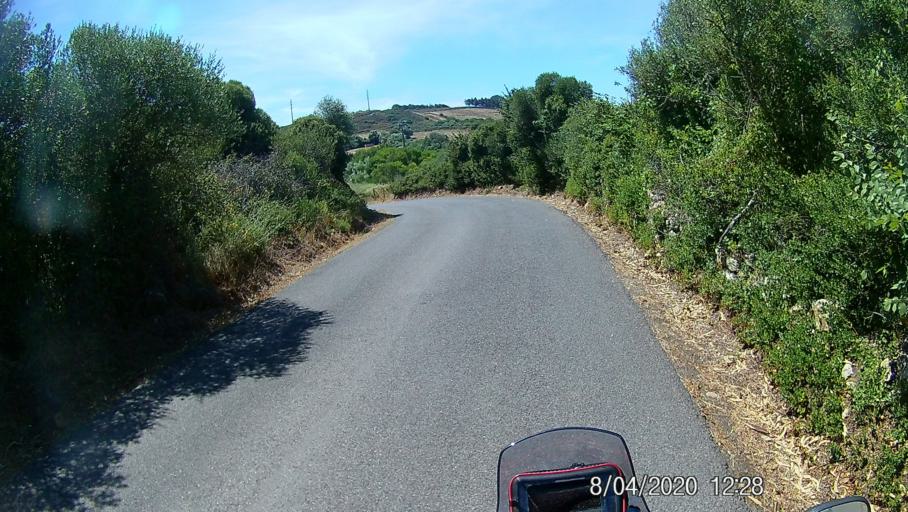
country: PT
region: Lisbon
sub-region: Sintra
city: Rio de Mouro
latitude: 38.7545
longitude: -9.3614
